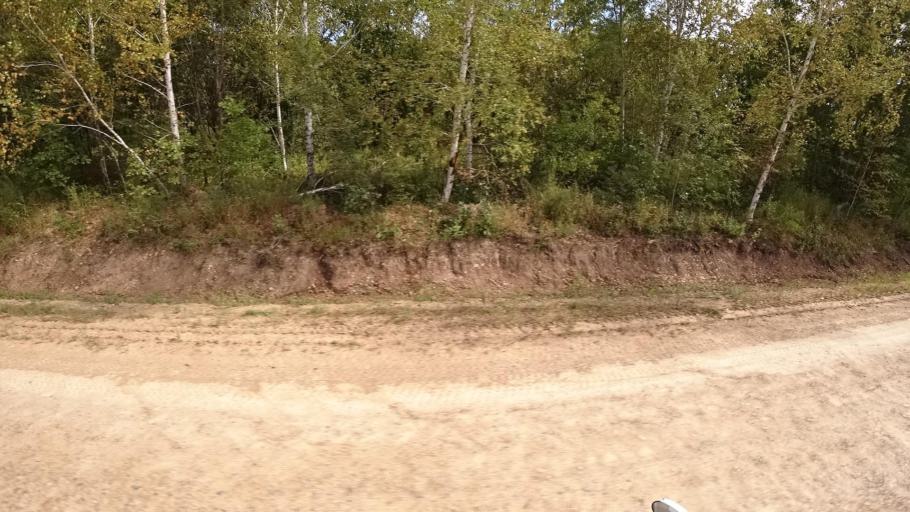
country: RU
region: Primorskiy
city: Yakovlevka
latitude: 44.7339
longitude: 133.6085
